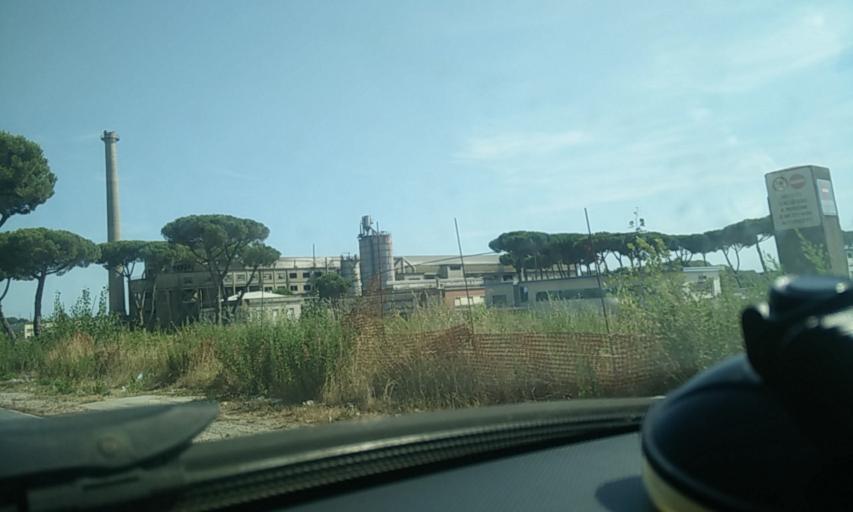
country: IT
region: Tuscany
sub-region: Provincia di Massa-Carrara
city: Carrara
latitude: 44.0456
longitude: 10.0824
